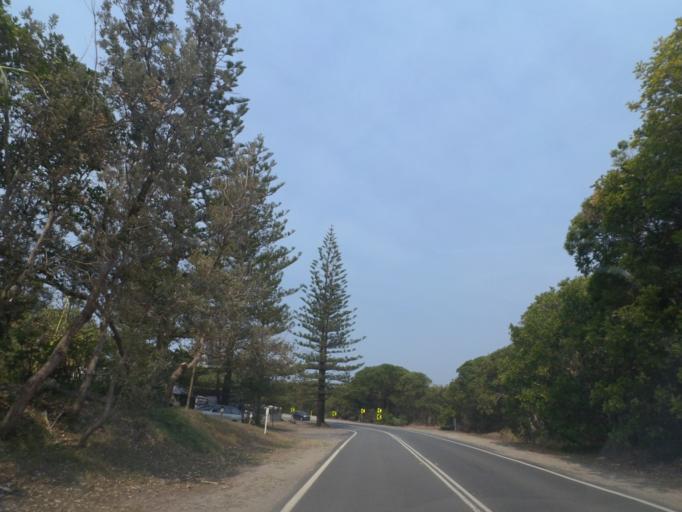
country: AU
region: New South Wales
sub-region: Tweed
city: Pottsville Beach
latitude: -28.4570
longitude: 153.5523
